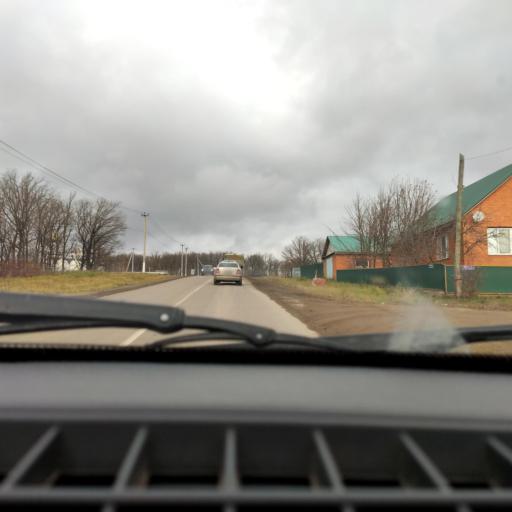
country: RU
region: Bashkortostan
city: Mikhaylovka
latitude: 54.8113
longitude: 55.8821
